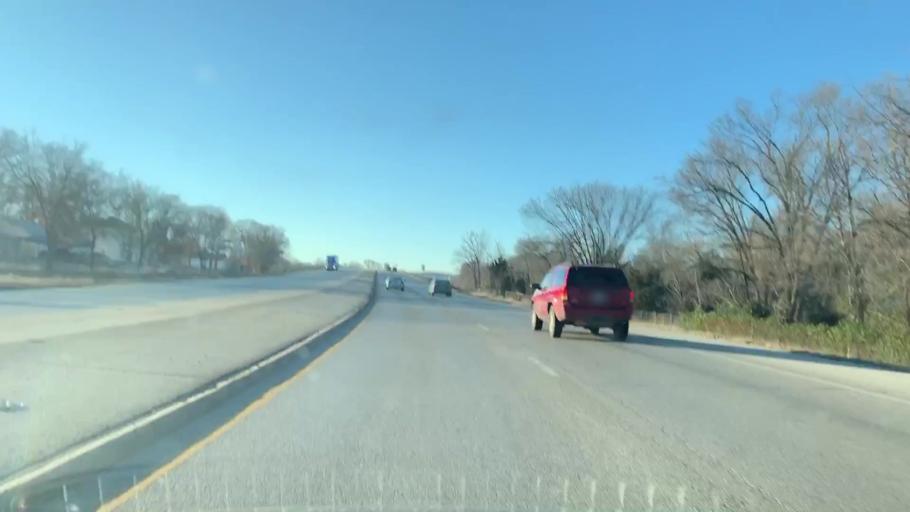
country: US
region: Kansas
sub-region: Bourbon County
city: Fort Scott
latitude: 37.8251
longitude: -94.7043
